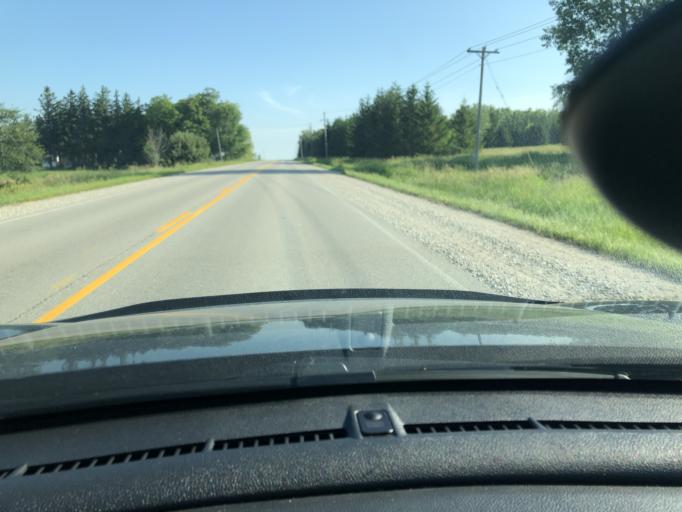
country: CA
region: Ontario
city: Stratford
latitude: 43.3968
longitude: -80.8375
